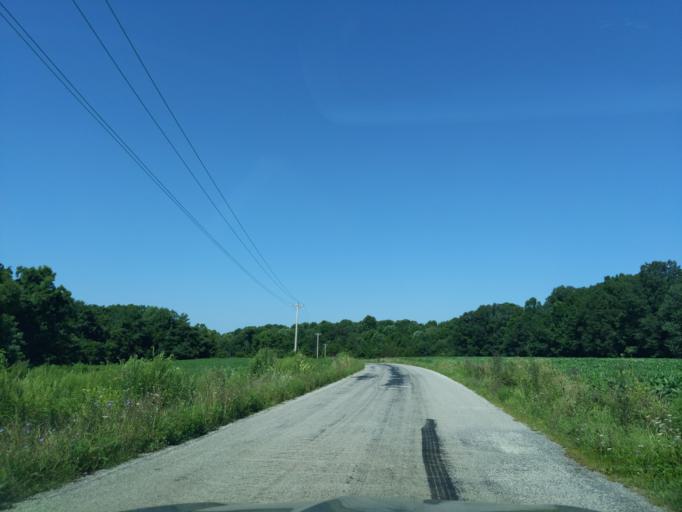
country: US
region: Indiana
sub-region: Ripley County
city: Osgood
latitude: 39.1126
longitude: -85.4382
